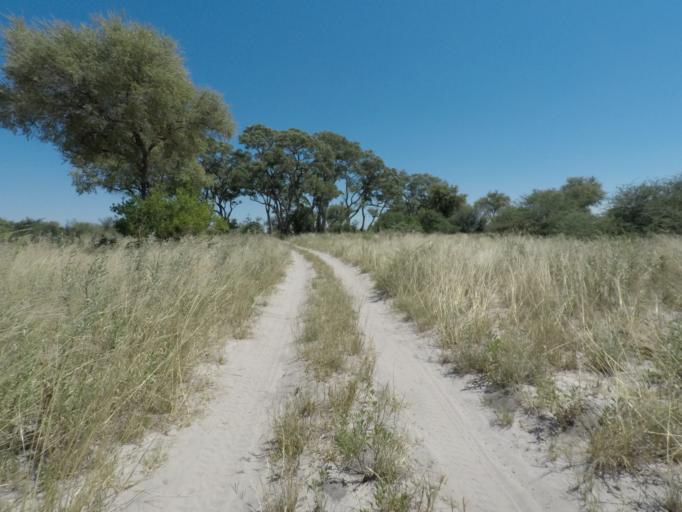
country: BW
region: North West
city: Maun
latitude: -19.4467
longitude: 23.5576
